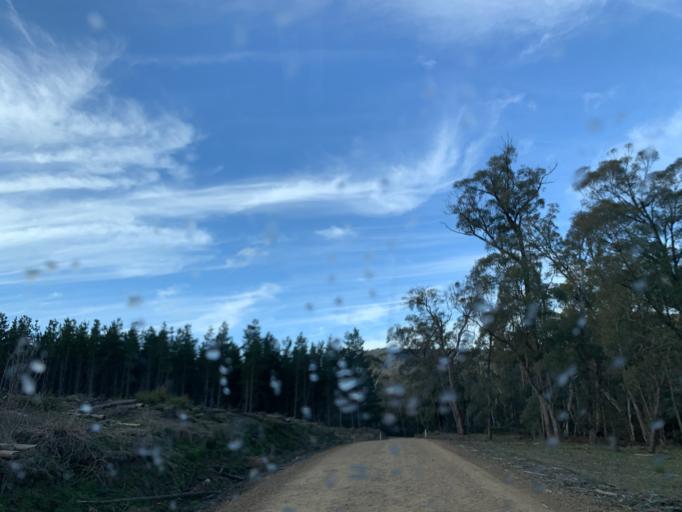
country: AU
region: Victoria
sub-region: Mansfield
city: Mansfield
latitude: -36.9262
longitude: 146.0973
